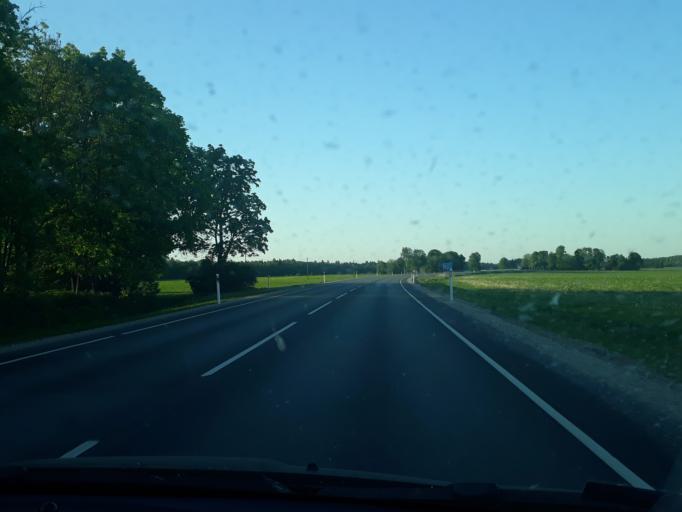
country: EE
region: Paernumaa
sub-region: Tootsi vald
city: Tootsi
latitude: 58.5485
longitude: 24.8485
